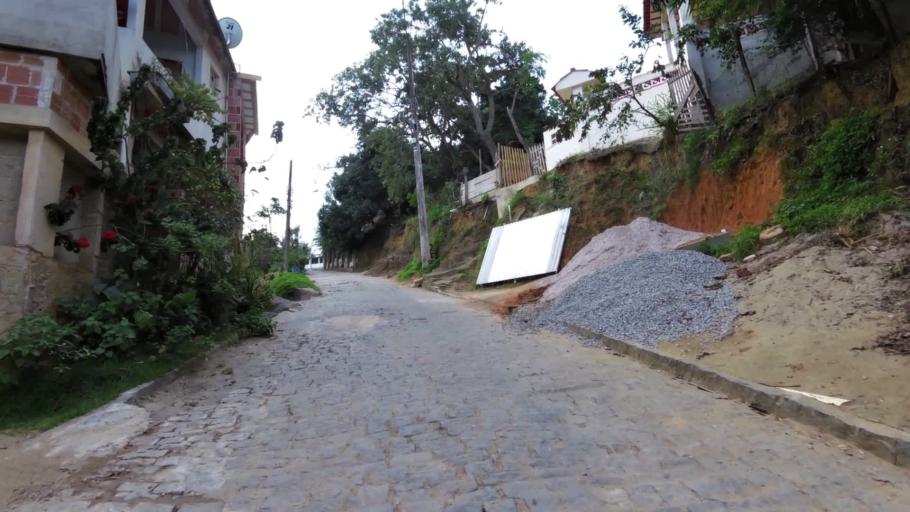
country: BR
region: Espirito Santo
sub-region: Piuma
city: Piuma
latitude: -20.8337
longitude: -40.7275
